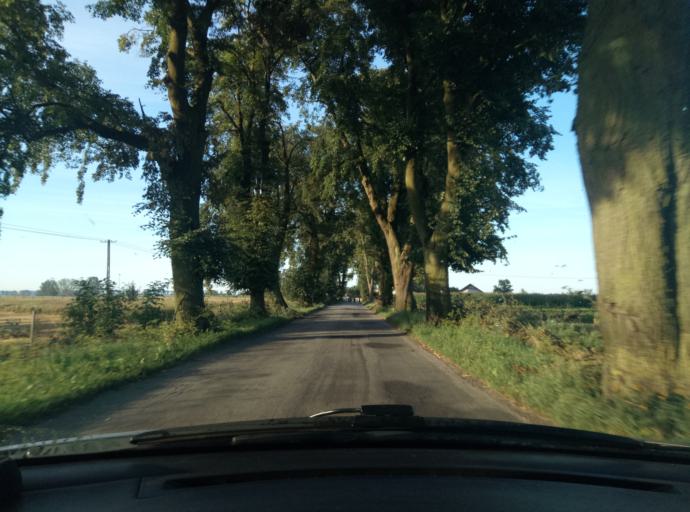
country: PL
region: Kujawsko-Pomorskie
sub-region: Powiat brodnicki
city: Jablonowo Pomorskie
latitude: 53.4122
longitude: 19.1757
